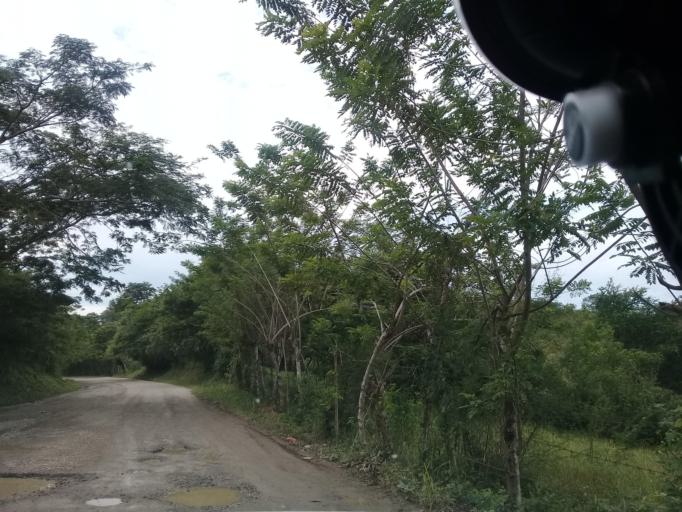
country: MX
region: Veracruz
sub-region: Chalma
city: San Pedro Coyutla
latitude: 21.2123
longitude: -98.3806
